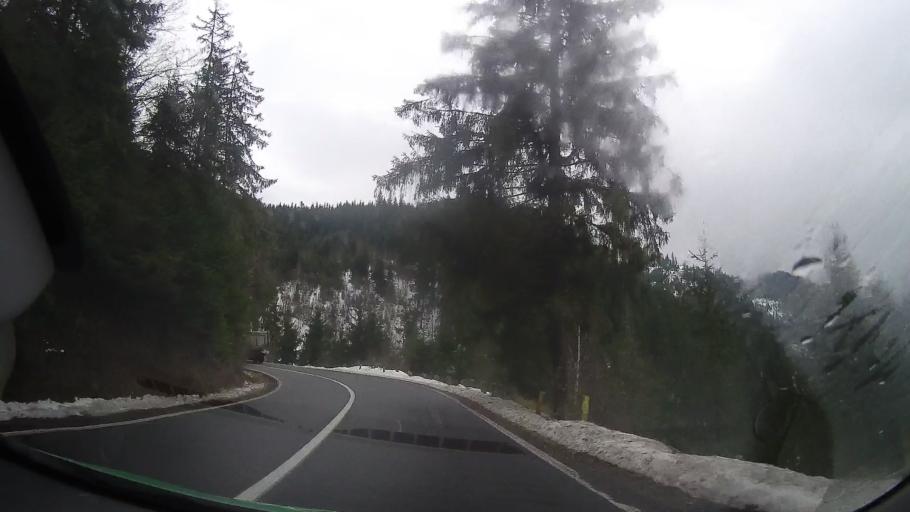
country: RO
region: Harghita
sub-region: Municipiul Gheorgheni
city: Gheorgheni
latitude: 46.7735
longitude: 25.7115
